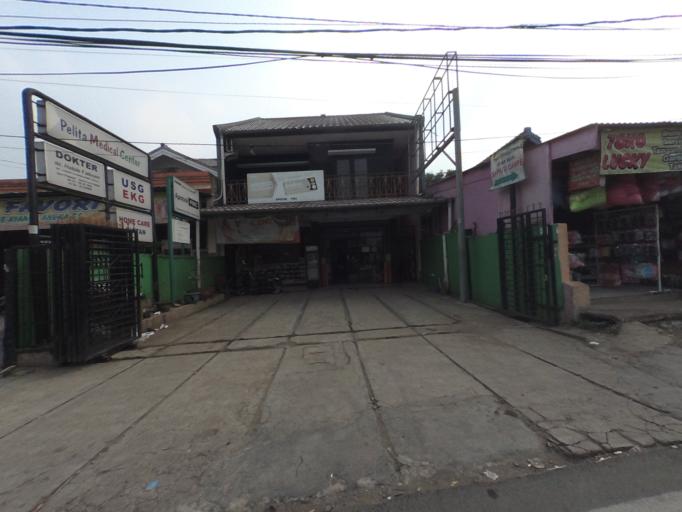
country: ID
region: West Java
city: Ciampea
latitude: -6.5547
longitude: 106.6977
